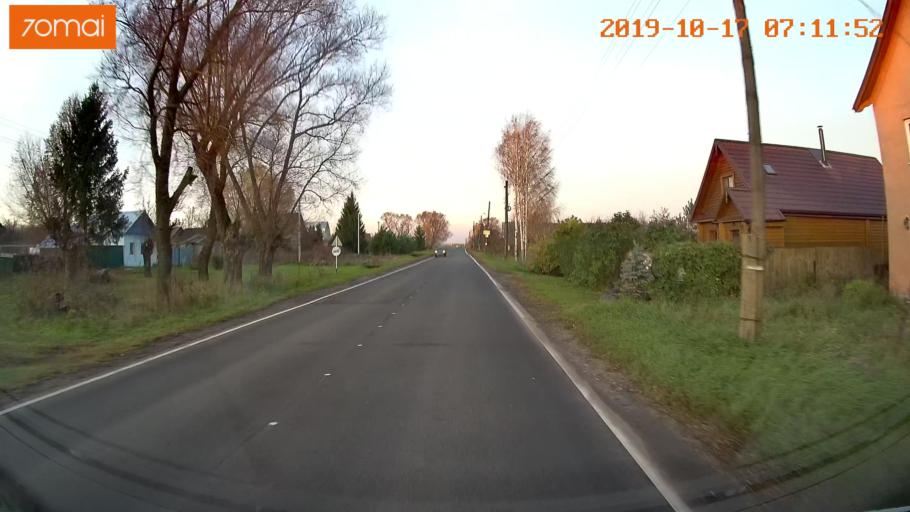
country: RU
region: Vladimir
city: Suzdal'
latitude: 56.4029
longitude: 40.3396
